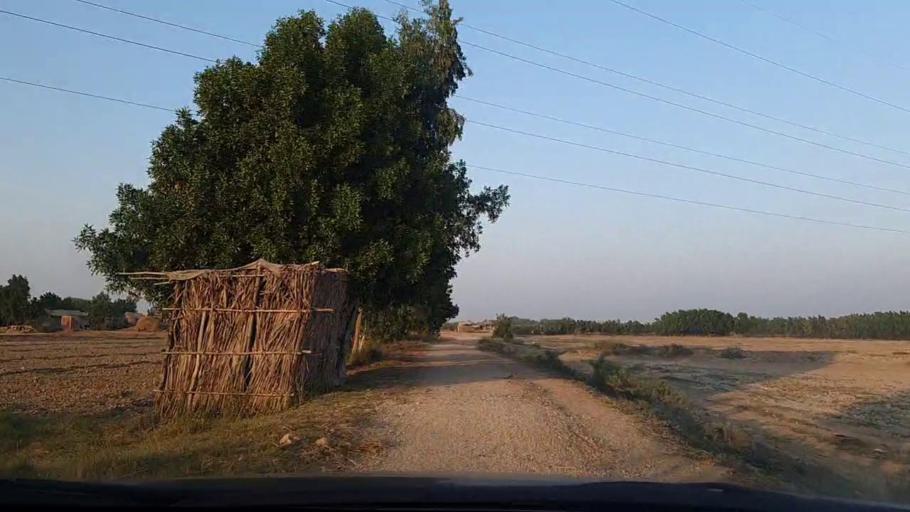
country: PK
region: Sindh
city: Mirpur Sakro
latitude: 24.5622
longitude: 67.6611
